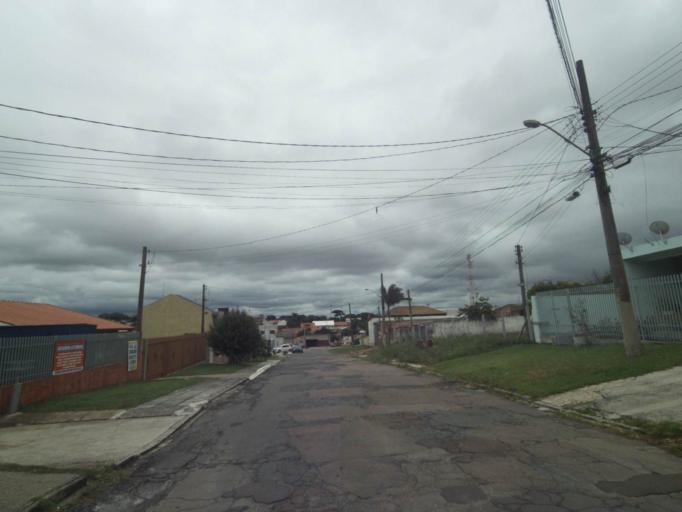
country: BR
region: Parana
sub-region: Curitiba
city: Curitiba
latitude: -25.4908
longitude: -49.3042
